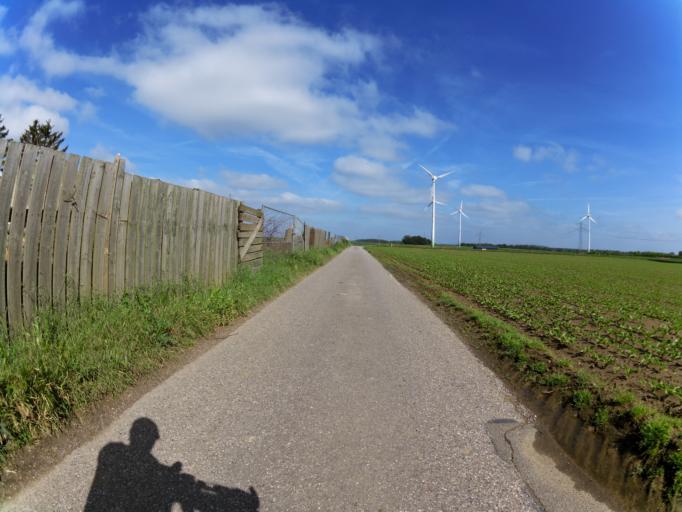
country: DE
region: North Rhine-Westphalia
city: Huckelhoven
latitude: 51.0045
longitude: 6.2205
